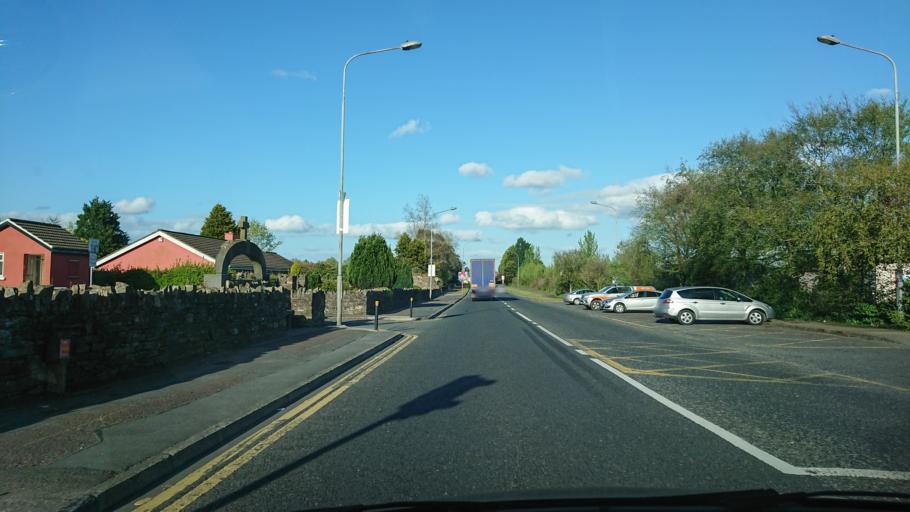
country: IE
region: Munster
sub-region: Waterford
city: Waterford
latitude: 52.2435
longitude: -7.1515
